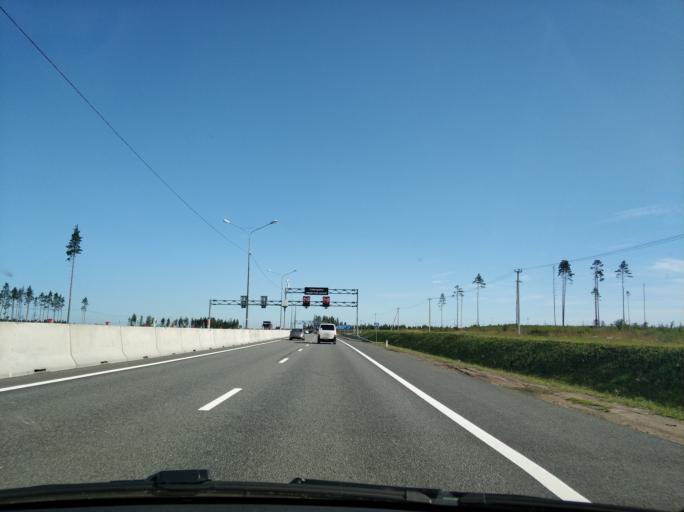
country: RU
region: Leningrad
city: Sosnovo
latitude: 60.4971
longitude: 30.1958
